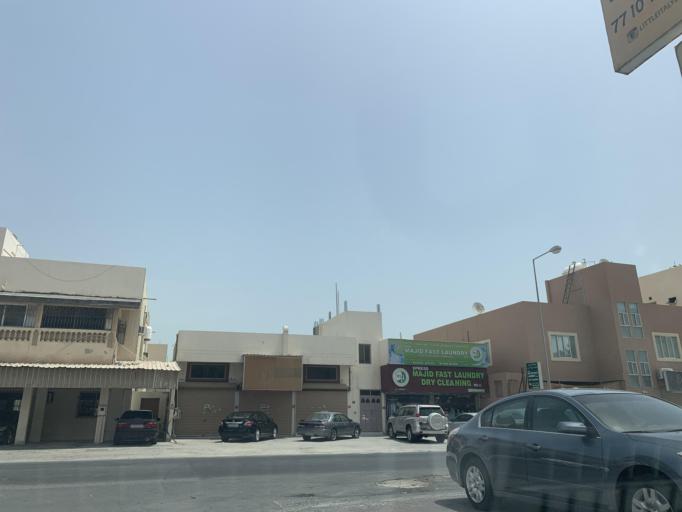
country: BH
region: Northern
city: Ar Rifa'
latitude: 26.1350
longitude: 50.5752
